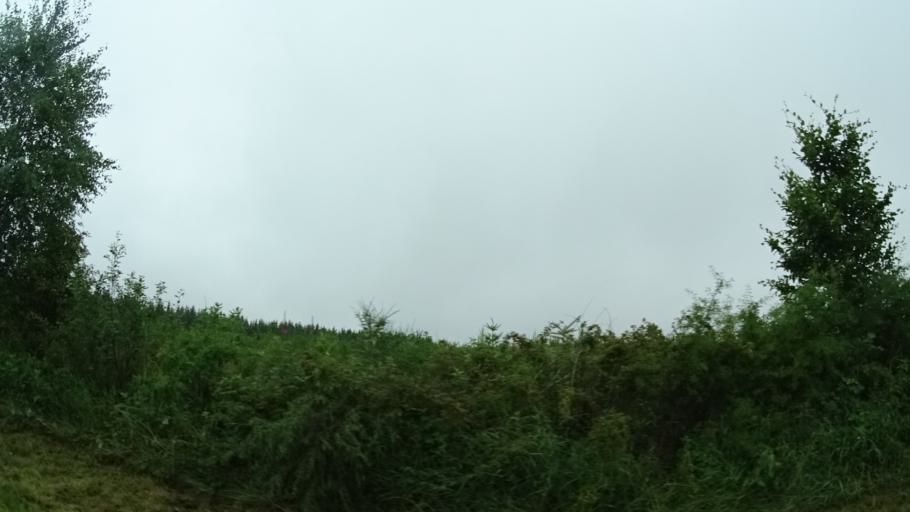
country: BE
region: Wallonia
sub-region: Province du Luxembourg
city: Leglise
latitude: 49.7908
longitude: 5.5391
